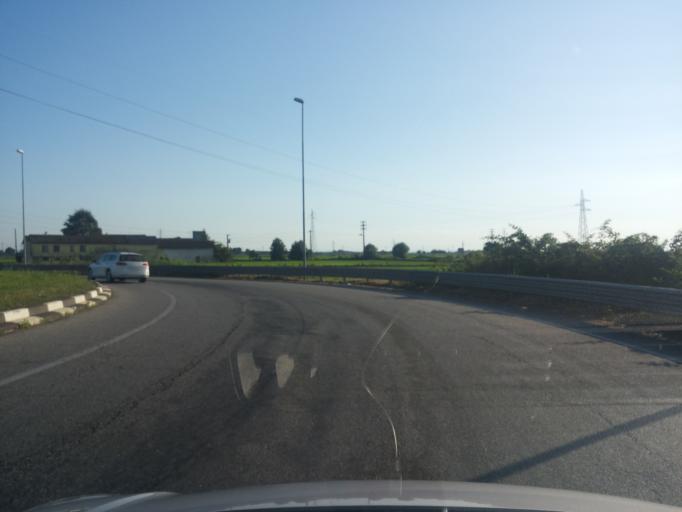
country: IT
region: Piedmont
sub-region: Provincia di Vercelli
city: Caresanablot
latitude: 45.3419
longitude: 8.3940
